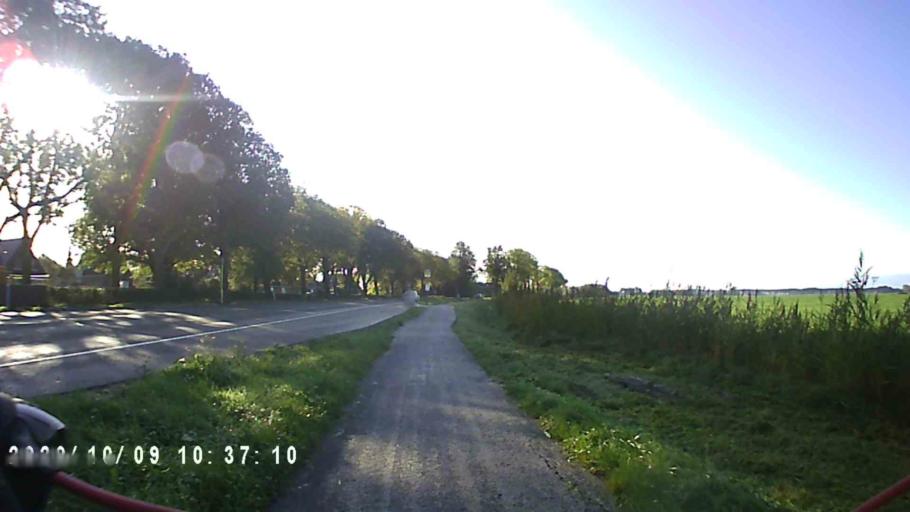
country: NL
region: Groningen
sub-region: Gemeente Winsum
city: Winsum
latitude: 53.2924
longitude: 6.5332
